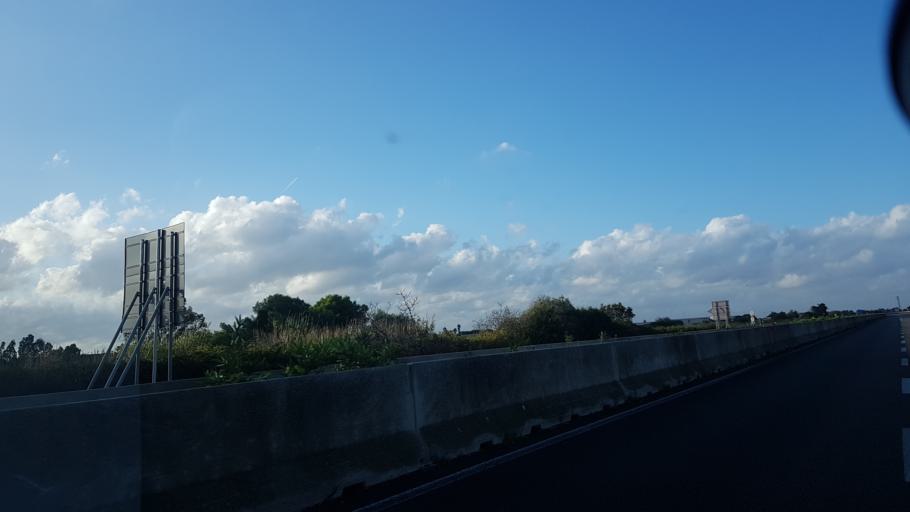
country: IT
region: Apulia
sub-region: Provincia di Lecce
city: Surbo
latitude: 40.3902
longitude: 18.1209
